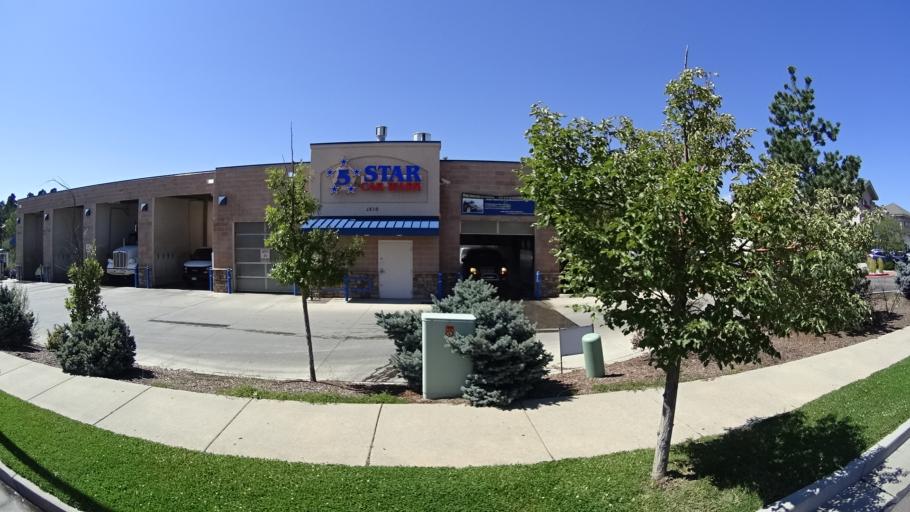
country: US
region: Colorado
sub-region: El Paso County
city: Cimarron Hills
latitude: 38.8549
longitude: -104.7235
